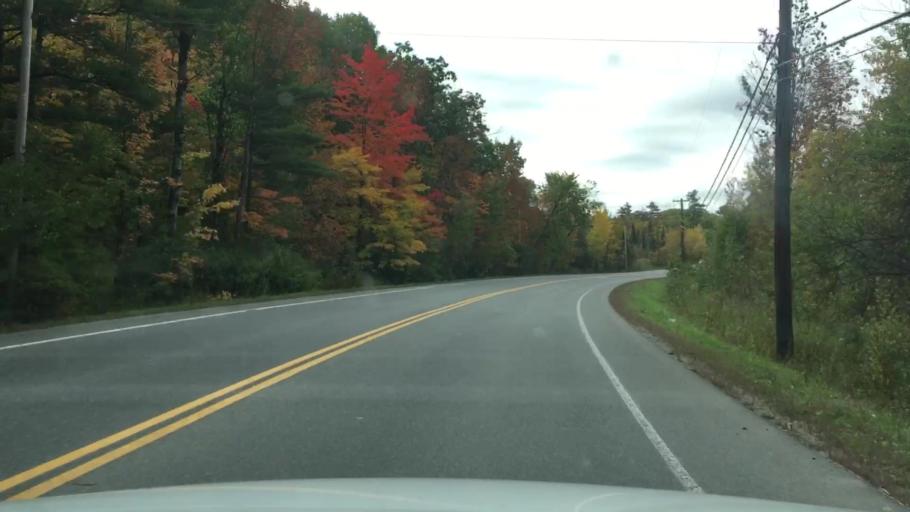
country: US
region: Maine
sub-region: Kennebec County
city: Waterville
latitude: 44.5579
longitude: -69.6695
